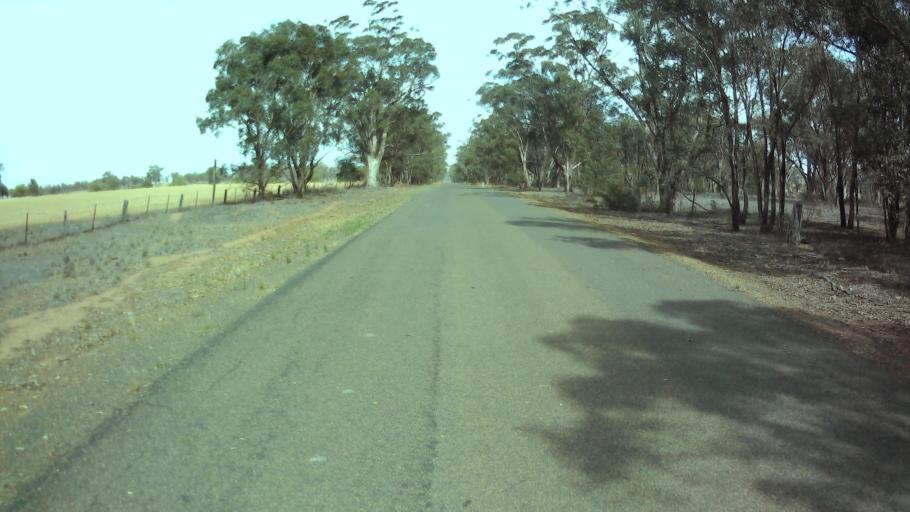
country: AU
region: New South Wales
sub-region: Weddin
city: Grenfell
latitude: -33.8081
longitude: 148.0608
